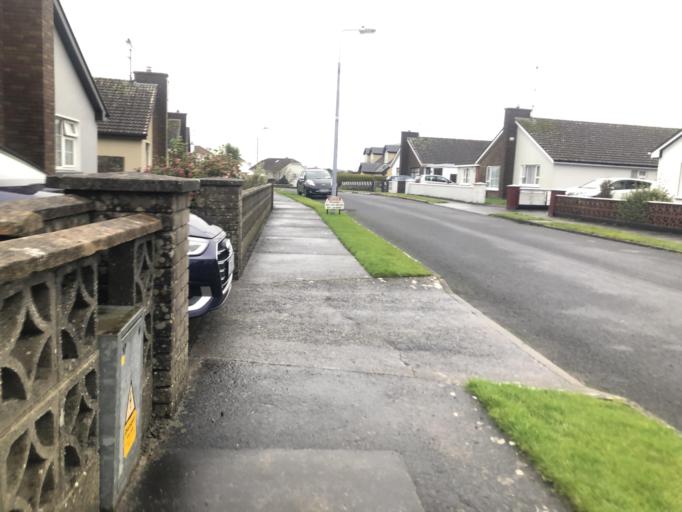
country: IE
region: Connaught
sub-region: County Galway
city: Tuam
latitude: 53.5106
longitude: -8.8680
